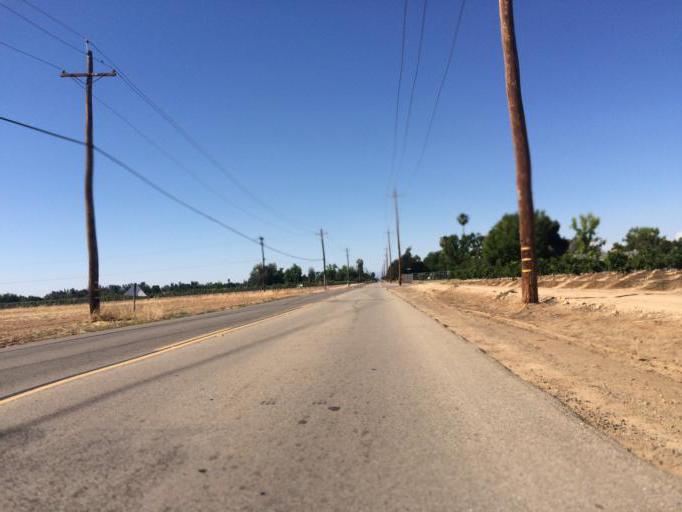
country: US
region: California
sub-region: Fresno County
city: Sanger
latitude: 36.7419
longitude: -119.6101
